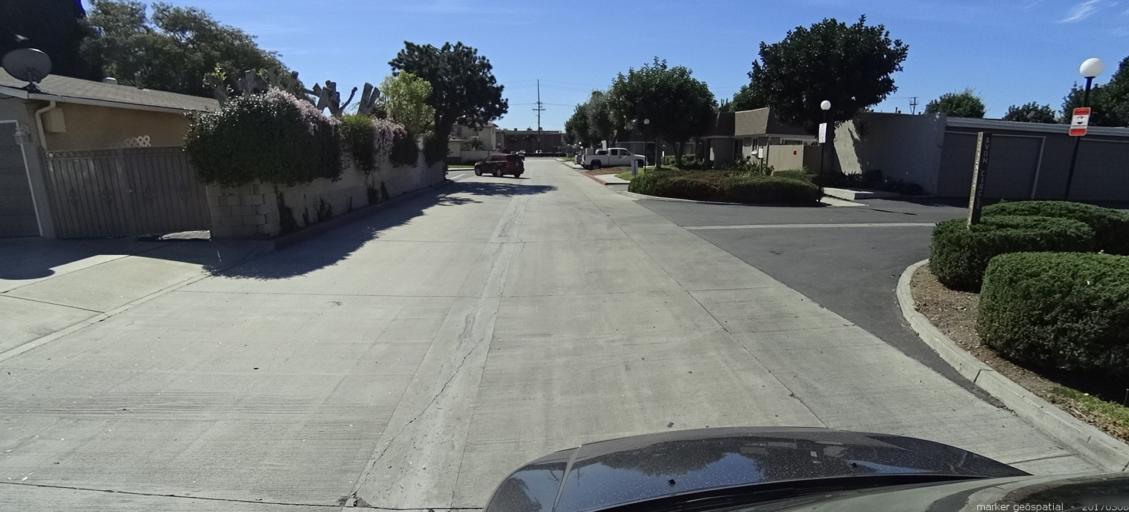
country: US
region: California
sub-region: Orange County
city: Stanton
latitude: 33.8192
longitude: -117.9568
